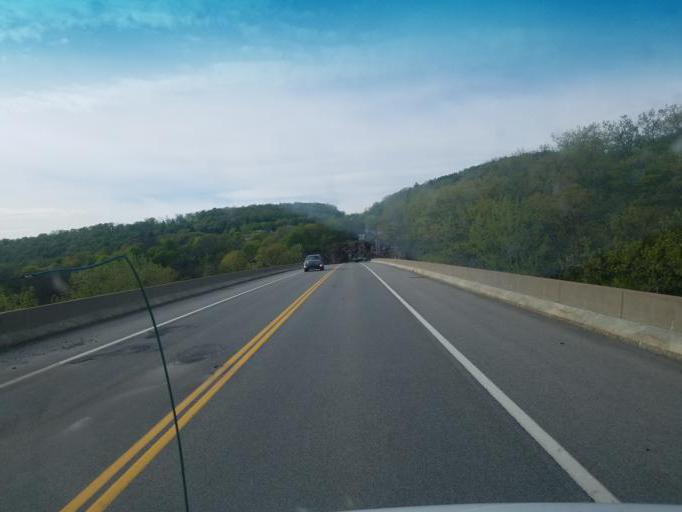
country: US
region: New York
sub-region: Herkimer County
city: Little Falls
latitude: 43.0408
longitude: -74.8458
